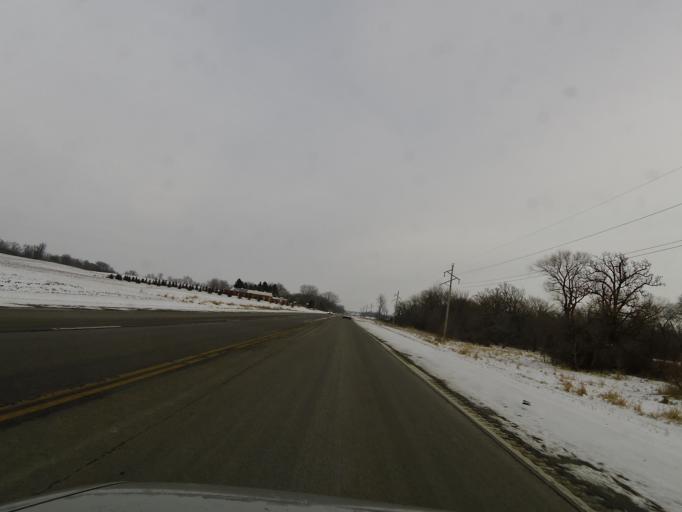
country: US
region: Minnesota
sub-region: Carver County
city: Mayer
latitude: 44.9058
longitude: -93.9040
